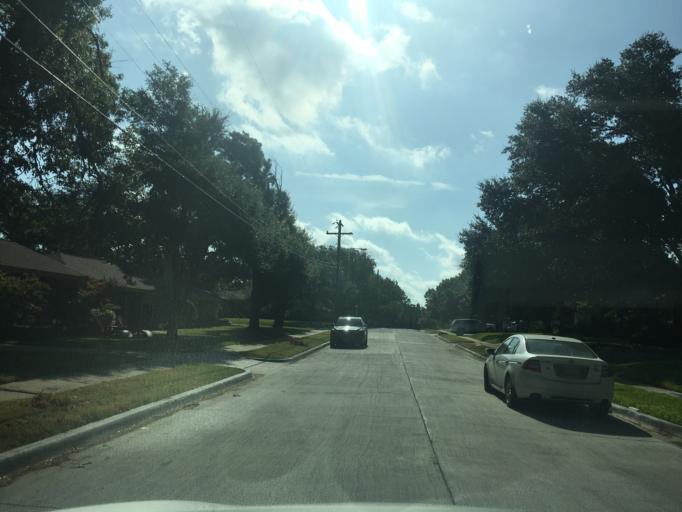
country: US
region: Texas
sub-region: Dallas County
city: Highland Park
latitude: 32.8358
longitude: -96.7472
